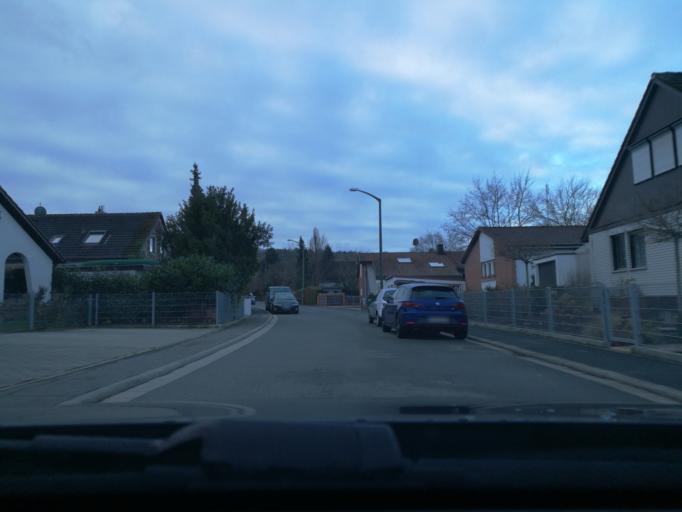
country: DE
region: Bavaria
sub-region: Upper Franconia
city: Langensendelbach
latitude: 49.6373
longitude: 11.0750
